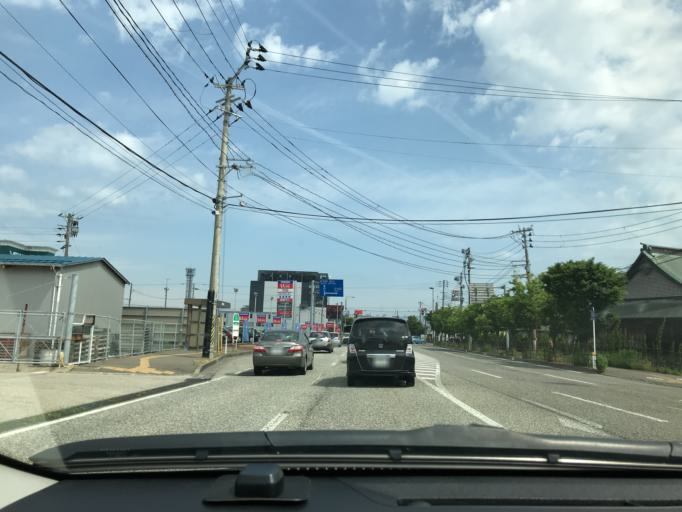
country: JP
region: Niigata
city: Niigata-shi
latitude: 37.8851
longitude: 139.0190
